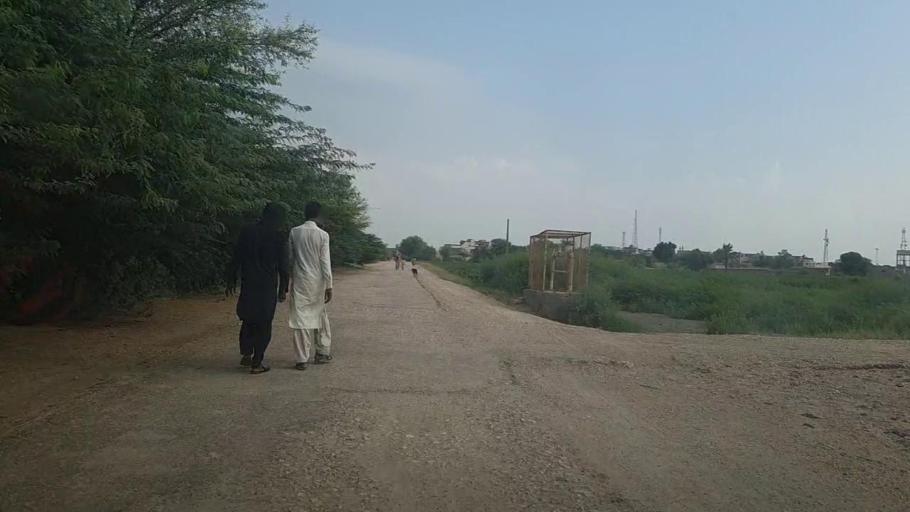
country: PK
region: Sindh
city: Mirpur Mathelo
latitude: 27.9217
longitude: 69.5201
